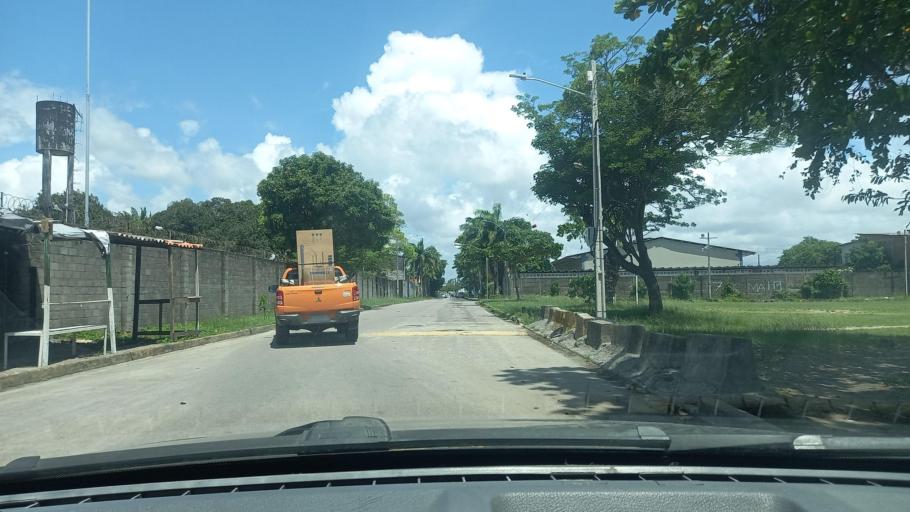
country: BR
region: Pernambuco
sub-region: Recife
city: Recife
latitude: -8.1020
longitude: -34.9093
